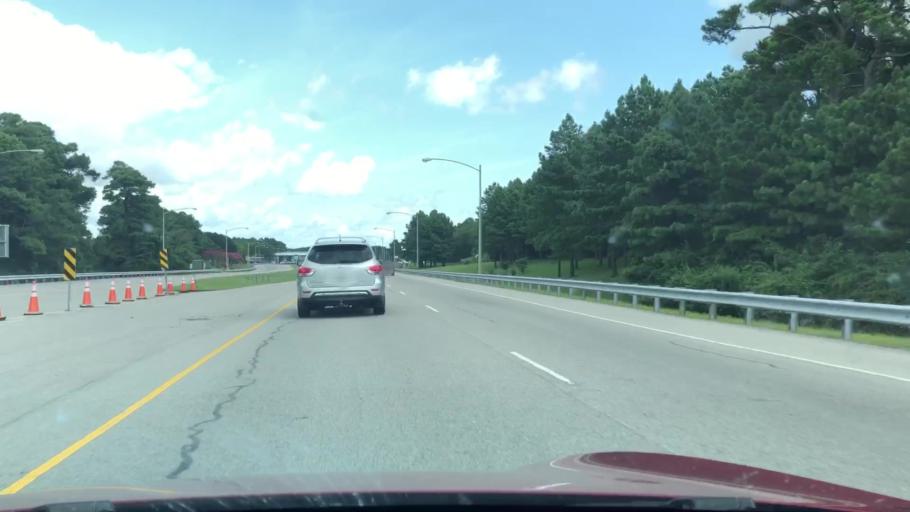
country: US
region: Virginia
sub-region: Northampton County
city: Cape Charles
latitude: 37.1278
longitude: -75.9675
